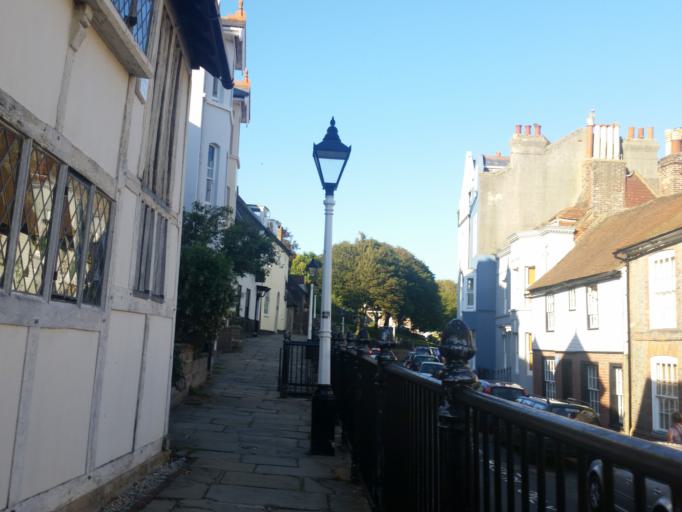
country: GB
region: England
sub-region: East Sussex
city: Hastings
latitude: 50.8593
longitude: 0.5935
